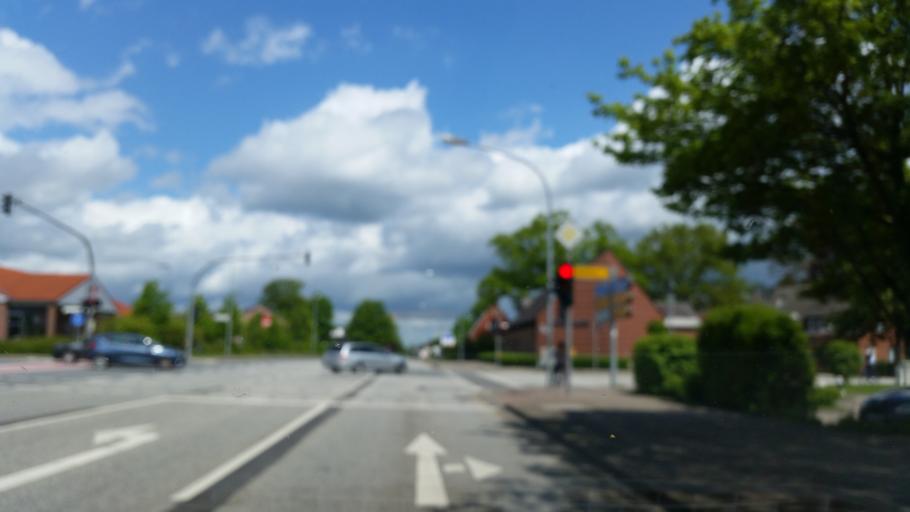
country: DE
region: Schleswig-Holstein
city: Norderstedt
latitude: 53.7228
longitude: 9.9980
